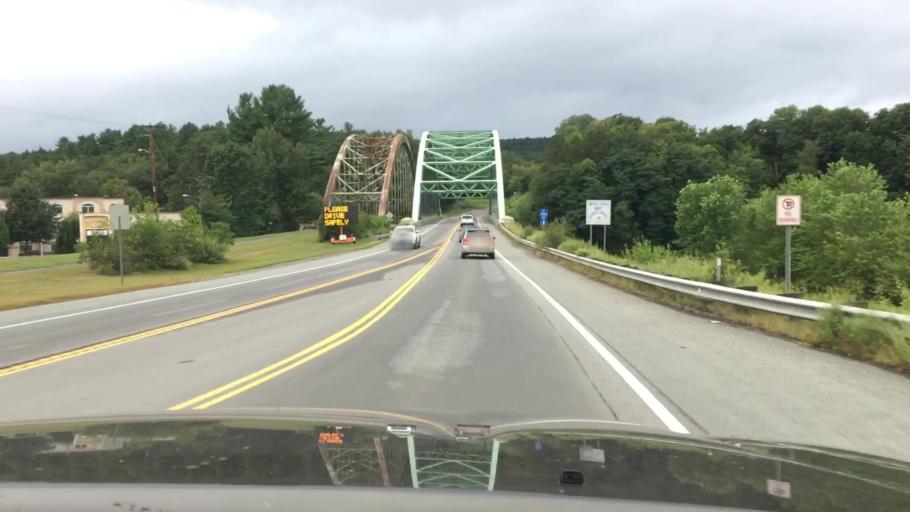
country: US
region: Vermont
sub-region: Windham County
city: Brattleboro
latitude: 42.8845
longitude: -72.5494
